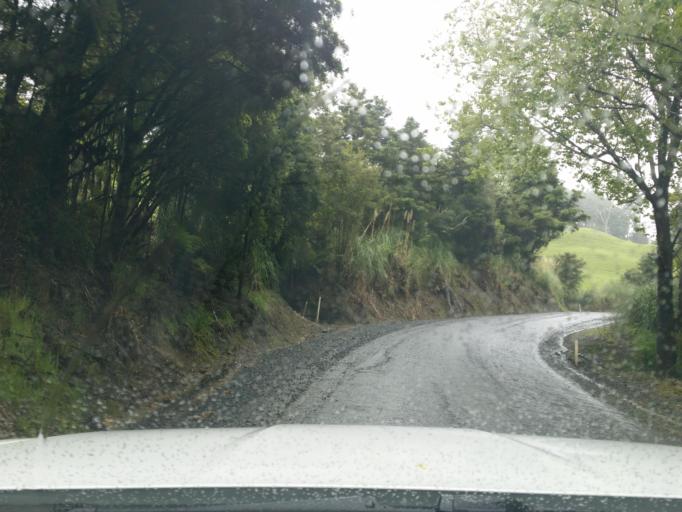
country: NZ
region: Northland
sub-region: Kaipara District
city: Dargaville
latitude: -35.7978
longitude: 173.9880
